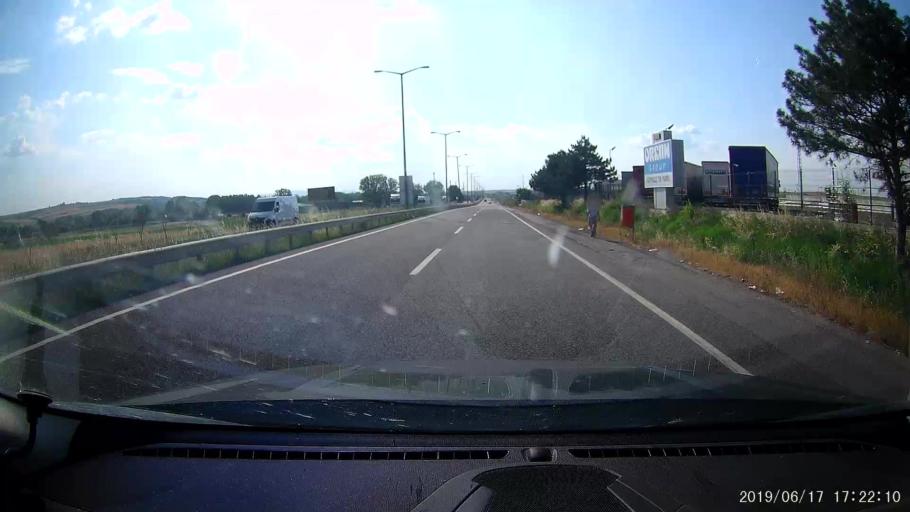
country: GR
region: East Macedonia and Thrace
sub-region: Nomos Evrou
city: Rizia
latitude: 41.7101
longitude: 26.3798
